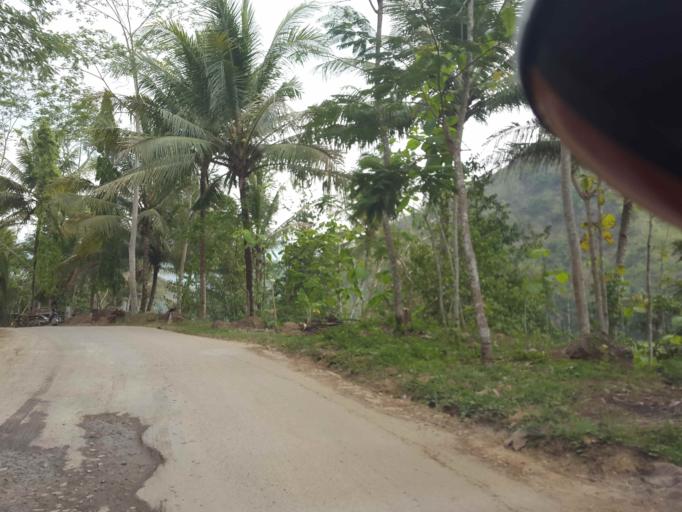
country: ID
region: East Java
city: Ploso
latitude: -8.0934
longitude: 111.1312
